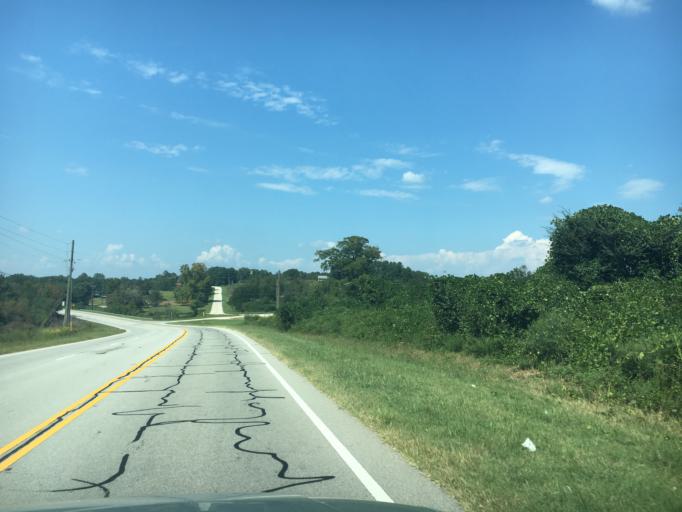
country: US
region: Georgia
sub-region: Franklin County
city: Lavonia
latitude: 34.4478
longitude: -83.0360
